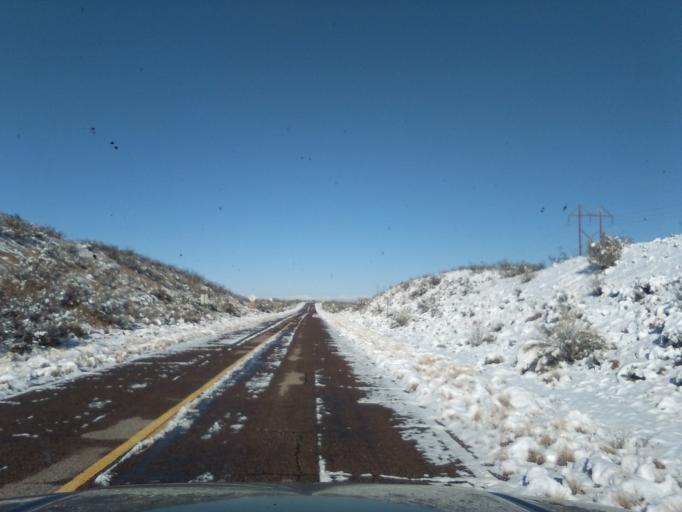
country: US
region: New Mexico
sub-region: Sierra County
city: Elephant Butte
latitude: 33.6099
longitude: -107.1486
